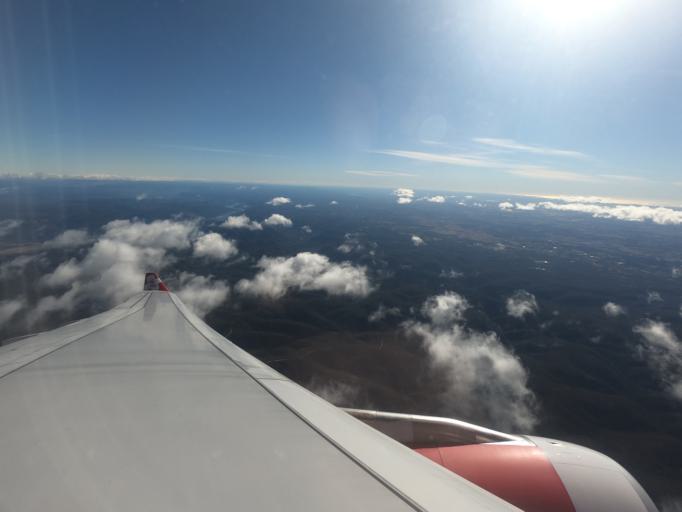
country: AU
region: New South Wales
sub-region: Wollondilly
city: Buxton
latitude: -34.2693
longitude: 150.4194
